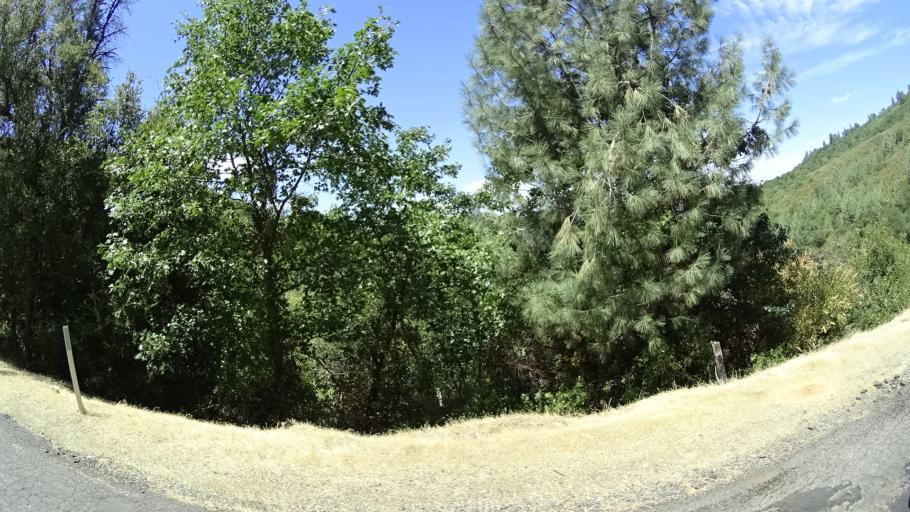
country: US
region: California
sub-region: Calaveras County
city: Forest Meadows
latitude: 38.1947
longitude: -120.4393
